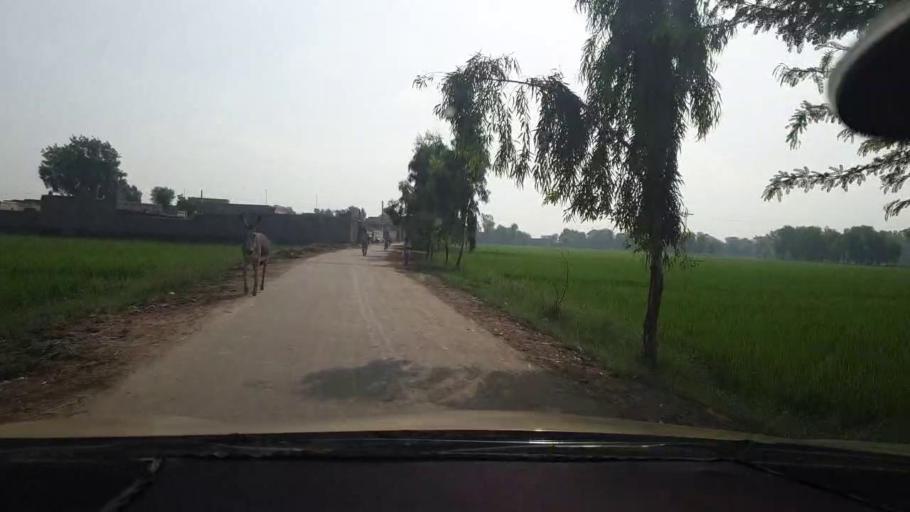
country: PK
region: Sindh
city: Goth Garelo
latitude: 27.4840
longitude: 68.0303
